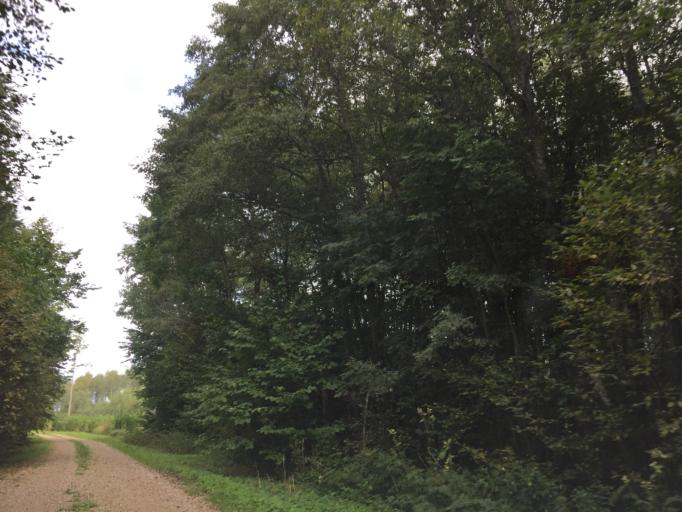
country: LV
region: Pargaujas
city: Stalbe
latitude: 57.4797
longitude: 24.9076
